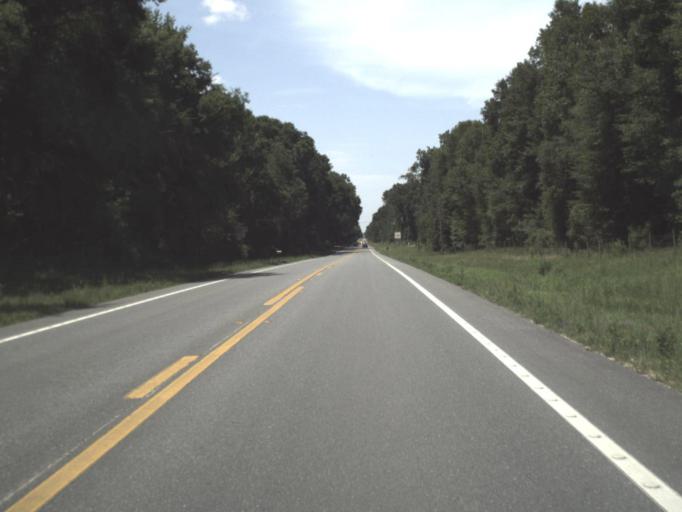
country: US
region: Florida
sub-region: Alachua County
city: High Springs
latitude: 29.8995
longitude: -82.8600
